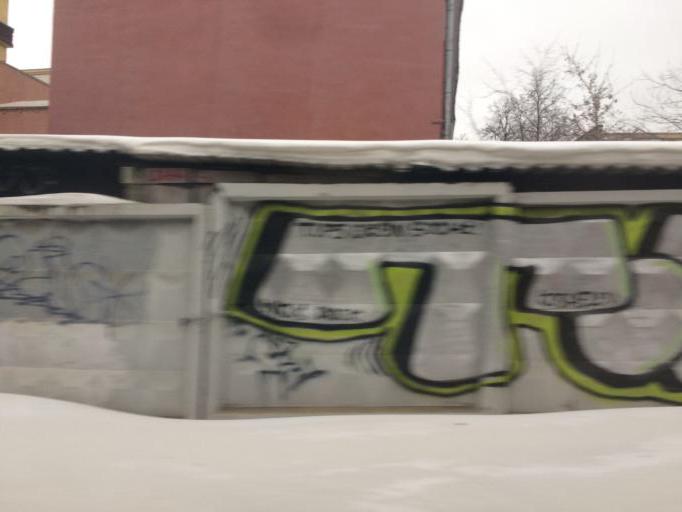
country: RU
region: Moscow
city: Sokol'niki
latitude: 55.7707
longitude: 37.6547
